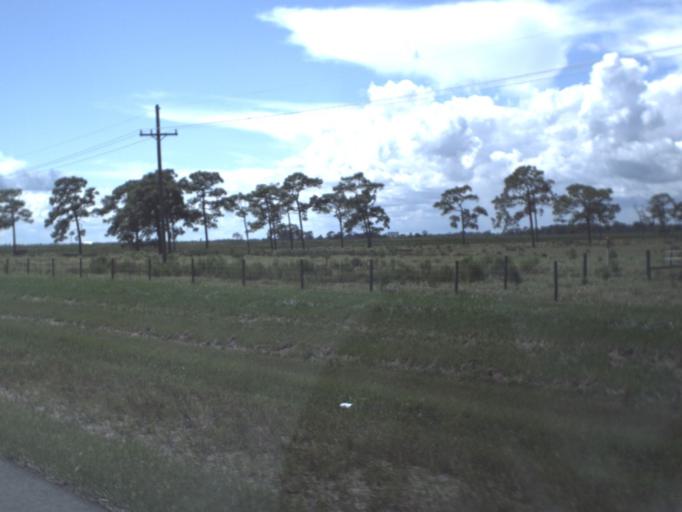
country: US
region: Florida
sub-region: Okeechobee County
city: Taylor Creek
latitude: 27.2821
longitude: -80.7100
